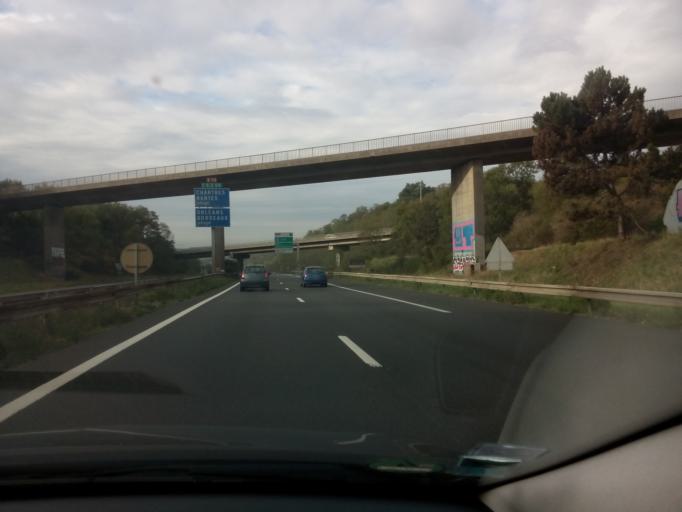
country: FR
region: Ile-de-France
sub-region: Departement de l'Essonne
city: Orsay
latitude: 48.6714
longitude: 2.1962
